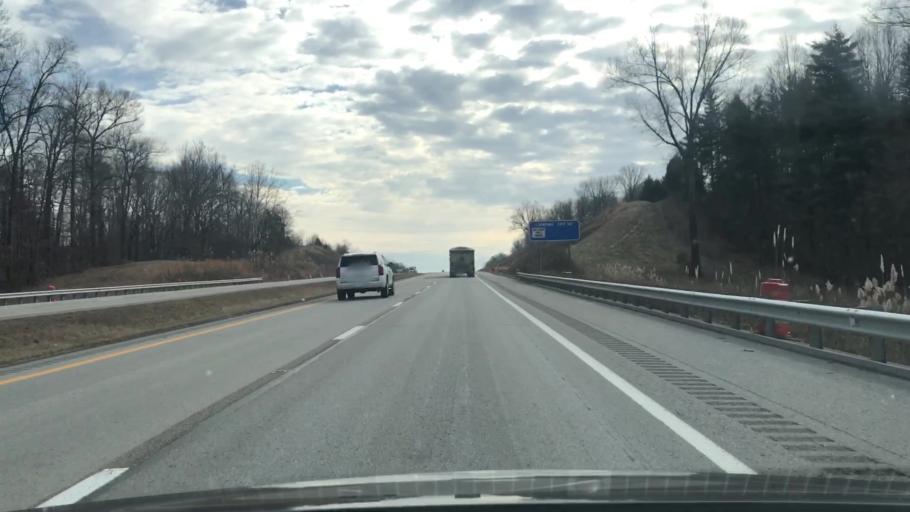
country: US
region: Kentucky
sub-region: Ohio County
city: Hartford
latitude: 37.4730
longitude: -86.8975
